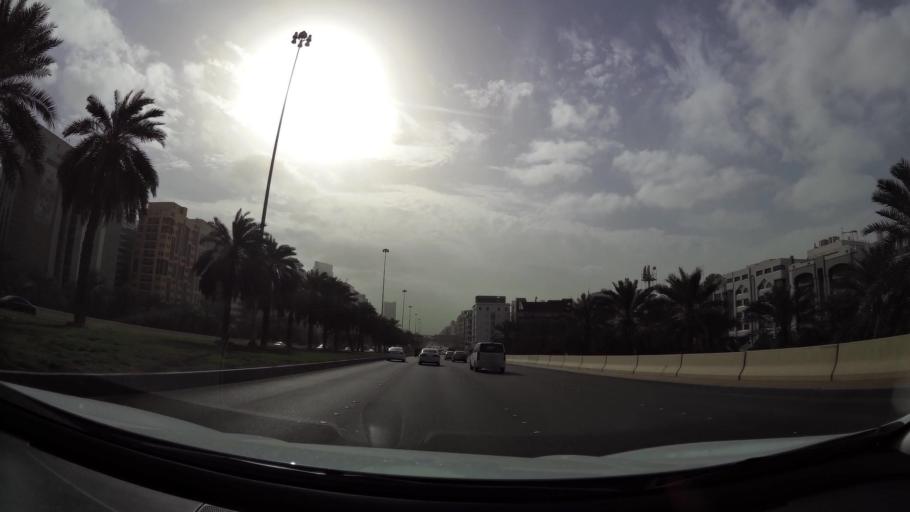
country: AE
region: Abu Dhabi
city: Abu Dhabi
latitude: 24.4659
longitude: 54.3826
